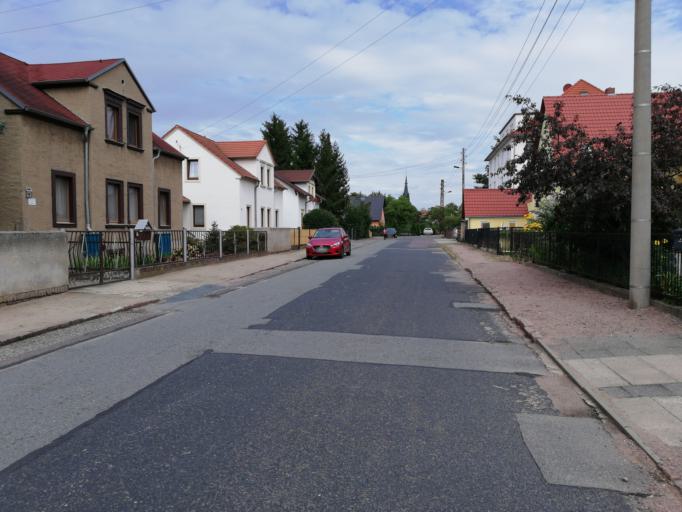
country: DE
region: Saxony
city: Weinbohla
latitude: 51.1580
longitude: 13.5669
